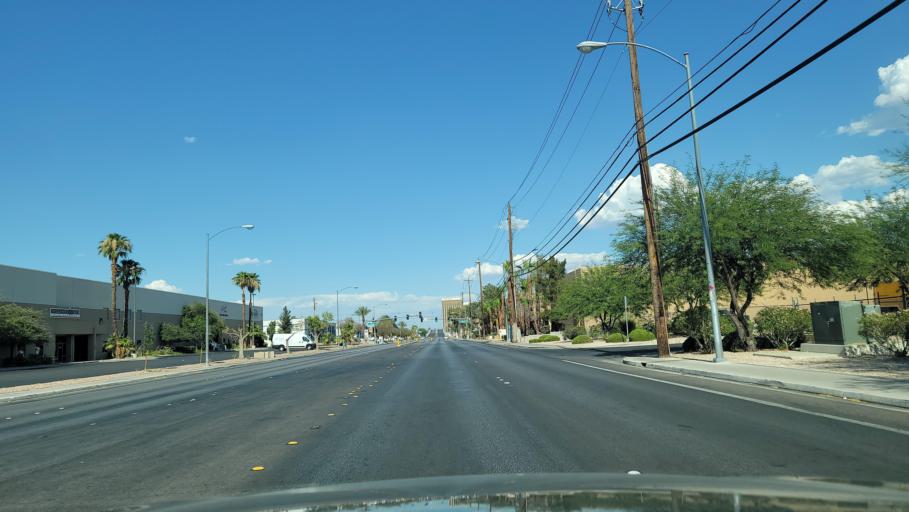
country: US
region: Nevada
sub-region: Clark County
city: Spring Valley
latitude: 36.0936
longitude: -115.2060
